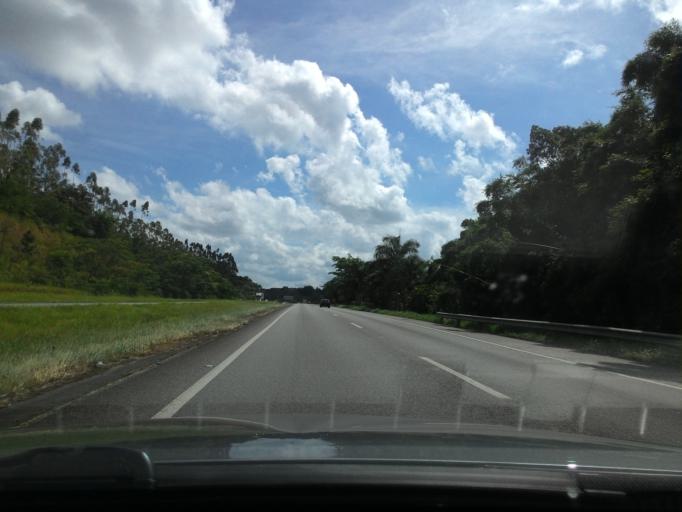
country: BR
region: Sao Paulo
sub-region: Registro
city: Registro
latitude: -24.5665
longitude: -47.8736
